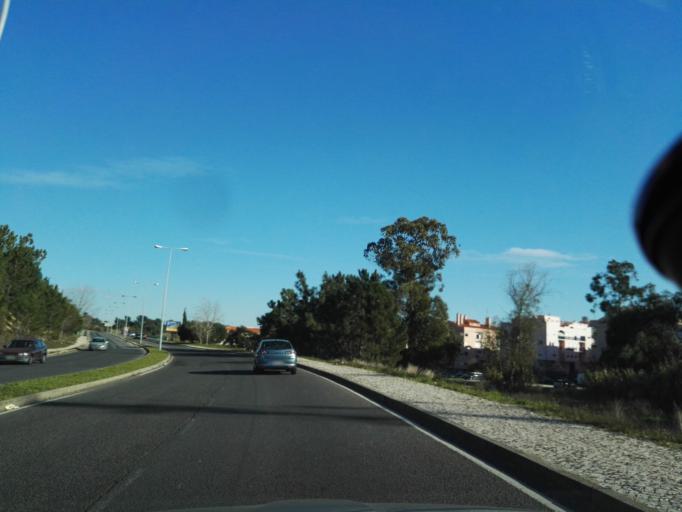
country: PT
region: Setubal
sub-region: Seixal
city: Corroios
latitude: 38.6449
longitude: -9.1555
